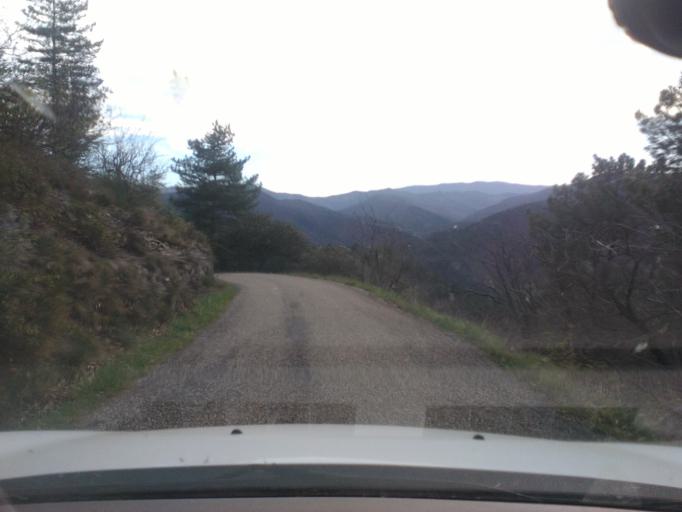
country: FR
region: Languedoc-Roussillon
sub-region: Departement du Gard
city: Saint-Jean-du-Gard
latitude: 44.1420
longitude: 3.7718
